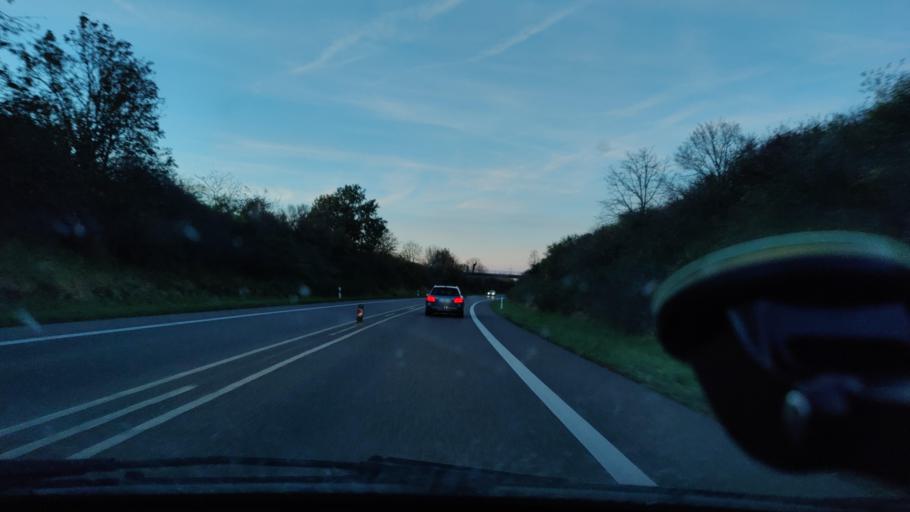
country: DE
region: North Rhine-Westphalia
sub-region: Regierungsbezirk Koln
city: Heinsberg
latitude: 51.0391
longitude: 6.1003
